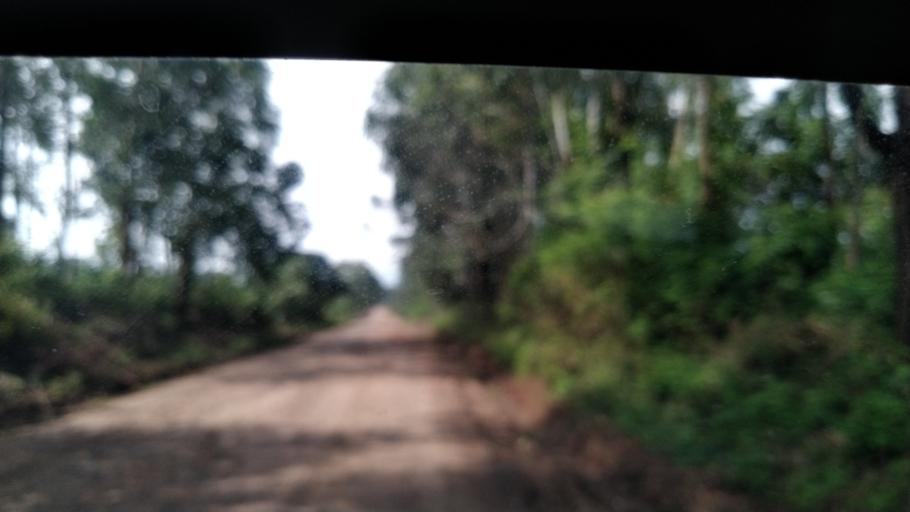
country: ET
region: Oromiya
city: Jima
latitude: 7.6655
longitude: 37.2451
